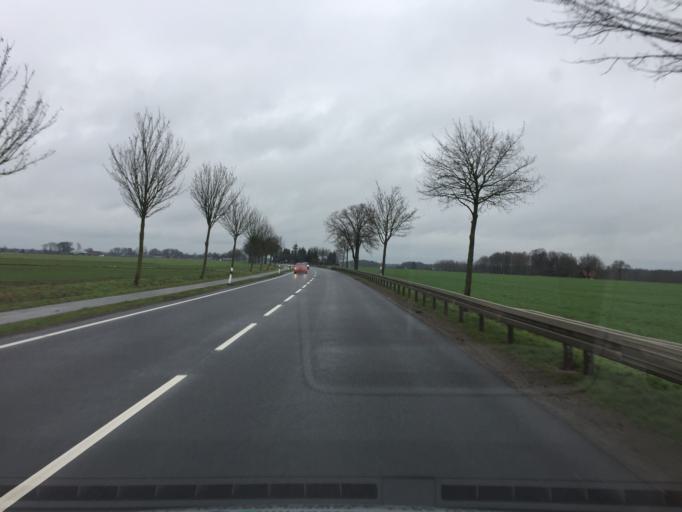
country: DE
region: Lower Saxony
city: Neuenkirchen
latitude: 52.7967
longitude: 8.7520
